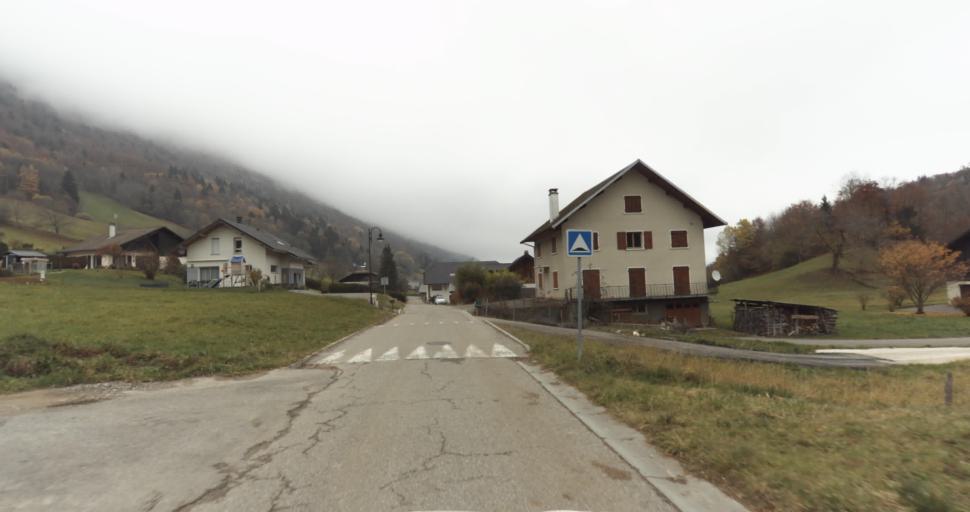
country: FR
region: Rhone-Alpes
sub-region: Departement de la Haute-Savoie
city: Doussard
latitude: 45.7909
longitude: 6.1901
